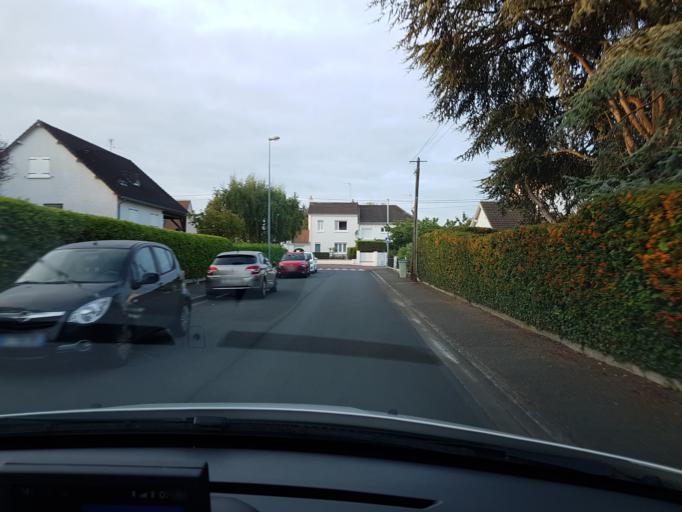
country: FR
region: Centre
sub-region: Departement d'Indre-et-Loire
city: Saint-Avertin
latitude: 47.3650
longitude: 0.7451
